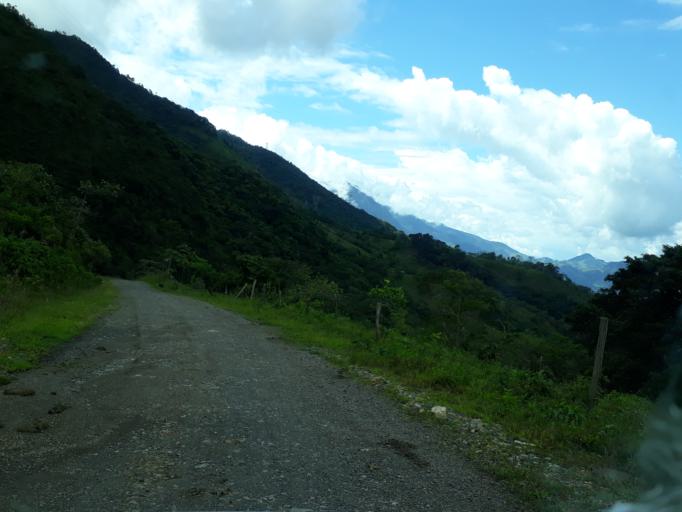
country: CO
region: Cundinamarca
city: Gachala
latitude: 4.7172
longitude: -73.3602
